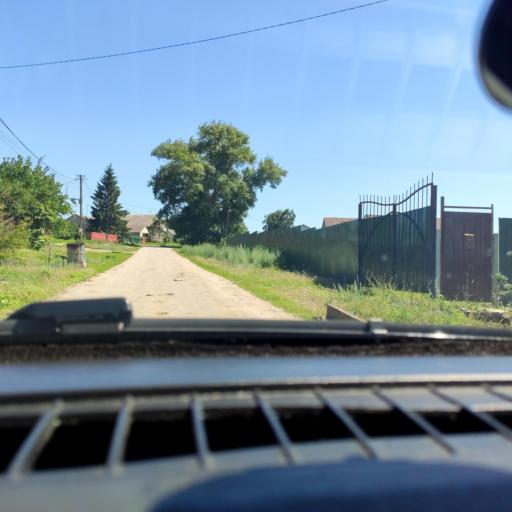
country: RU
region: Voronezj
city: Podgornoye
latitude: 51.8009
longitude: 39.1367
